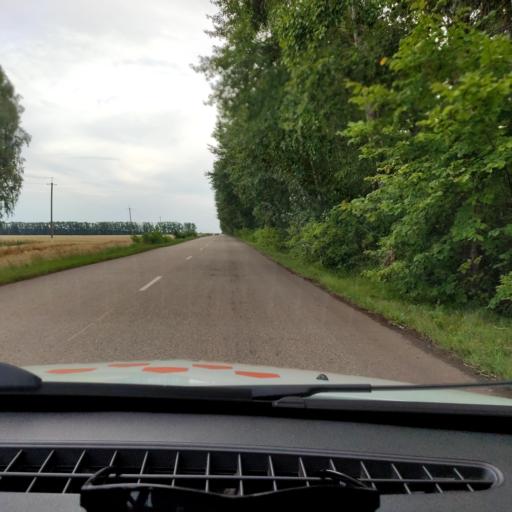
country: RU
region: Bashkortostan
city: Avdon
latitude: 54.5206
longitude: 55.6330
